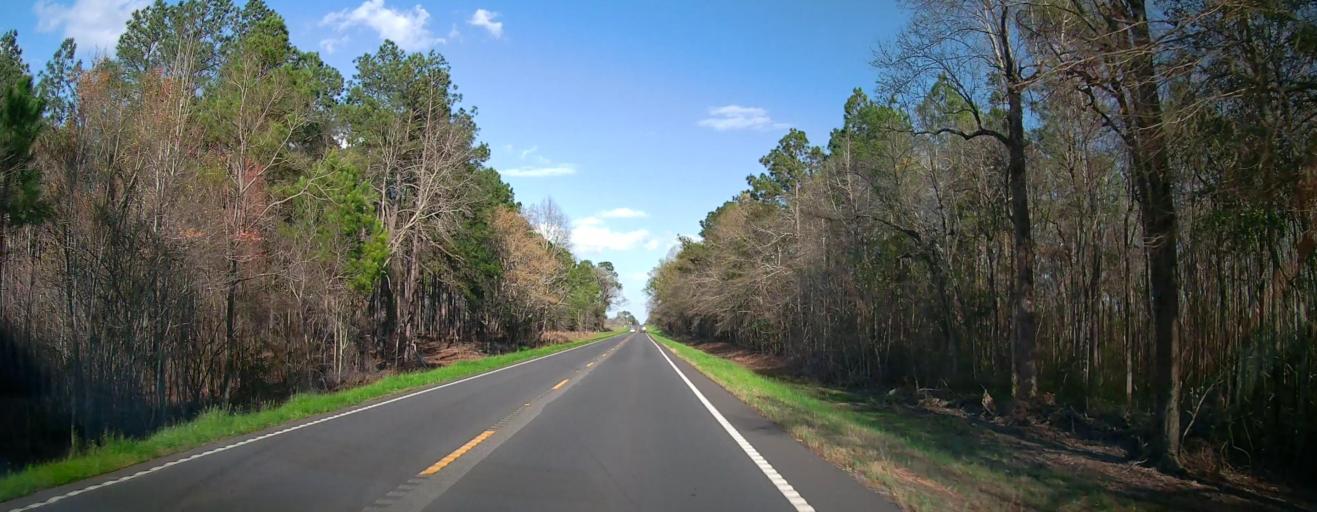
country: US
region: Georgia
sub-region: Montgomery County
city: Mount Vernon
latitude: 32.1848
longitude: -82.5378
